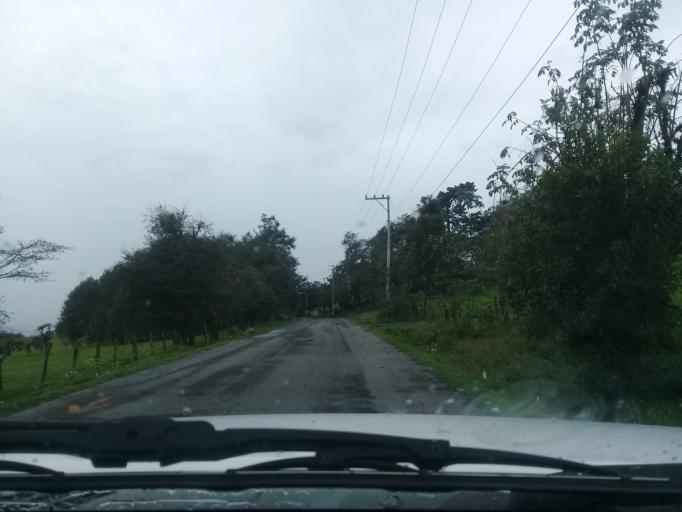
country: MX
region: Veracruz
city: Rafael Lucio
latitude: 19.6095
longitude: -97.0042
